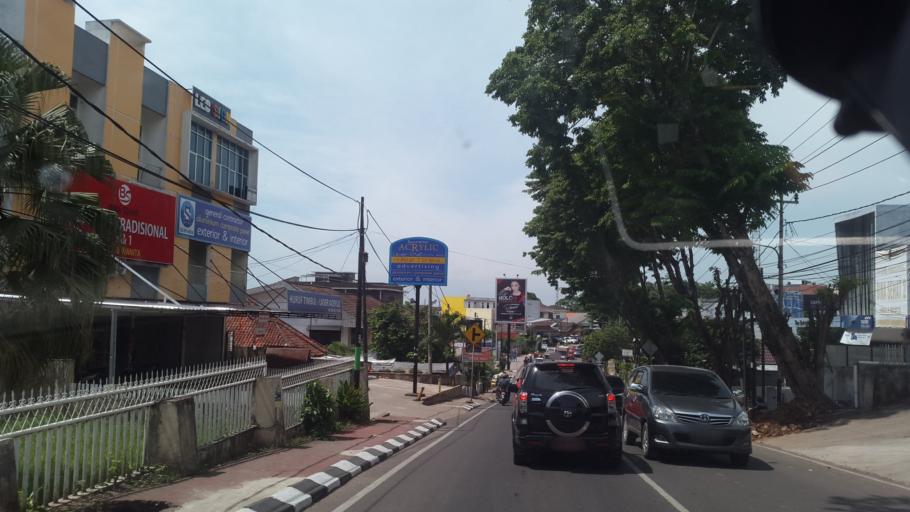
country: ID
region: South Sumatra
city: Plaju
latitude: -2.9887
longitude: 104.7389
